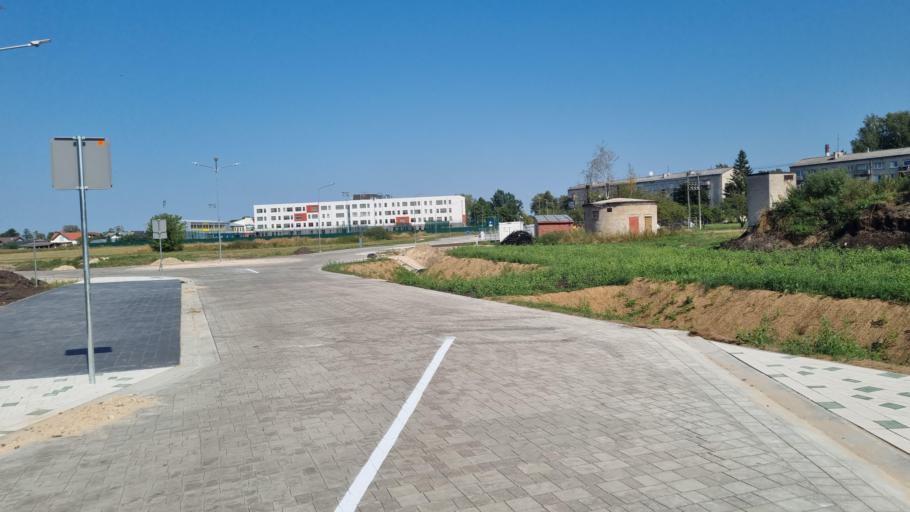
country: LV
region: Marupe
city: Marupe
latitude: 56.8816
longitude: 24.0628
